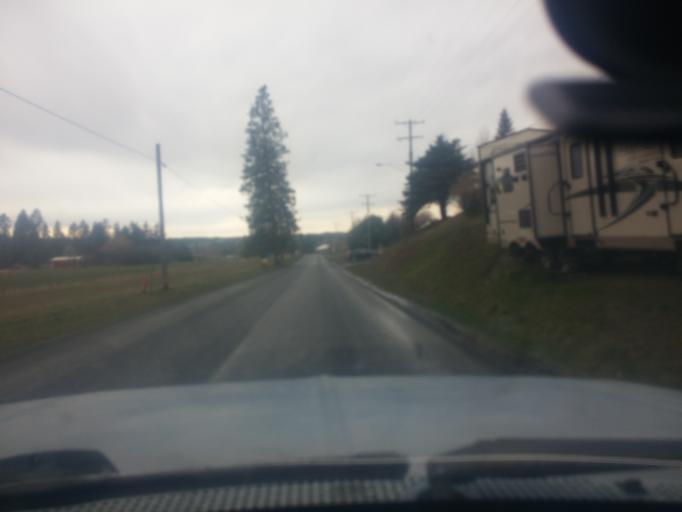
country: US
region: Idaho
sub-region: Latah County
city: Moscow
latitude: 46.9281
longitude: -116.8932
